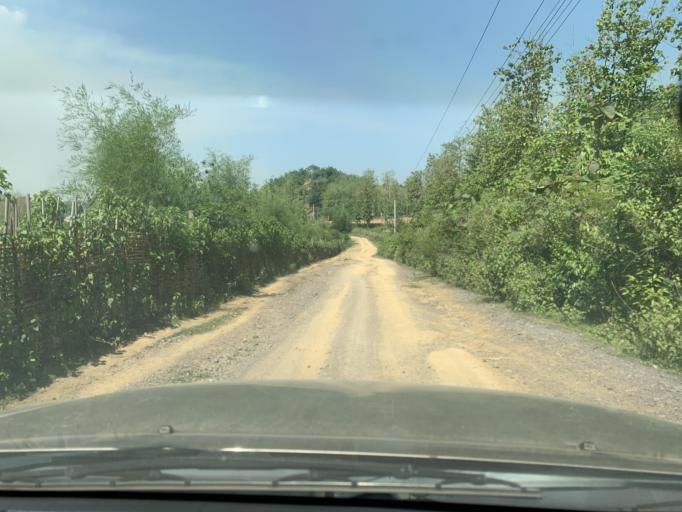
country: LA
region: Louangphabang
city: Louangphabang
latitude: 19.9265
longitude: 102.2741
